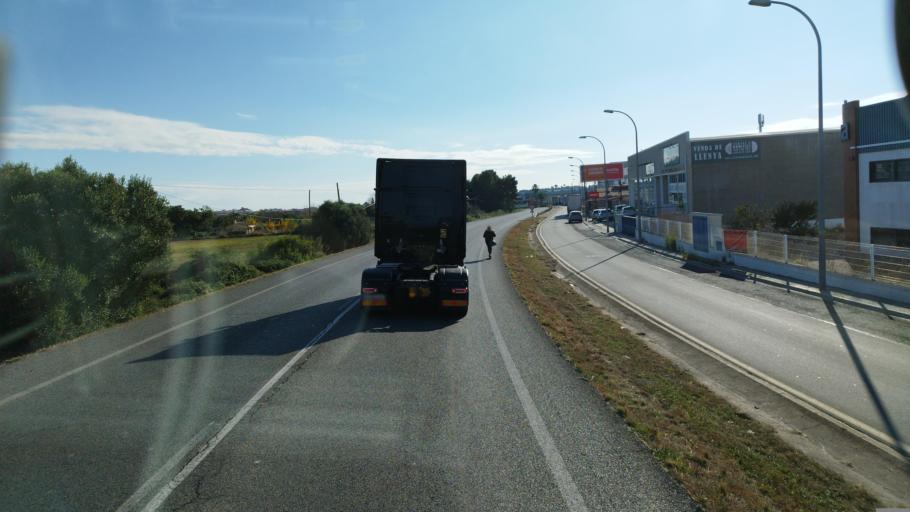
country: ES
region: Catalonia
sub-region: Provincia de Tarragona
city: Torredembarra
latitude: 41.1553
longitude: 1.3931
